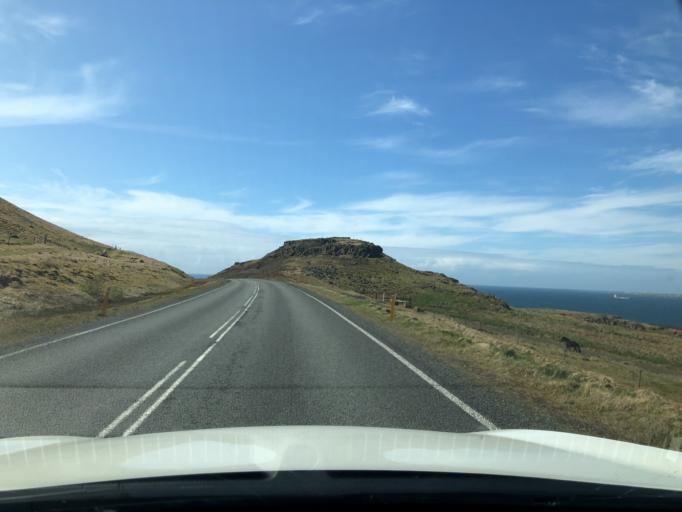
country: IS
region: Capital Region
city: Reykjavik
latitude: 64.2844
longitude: -21.8234
